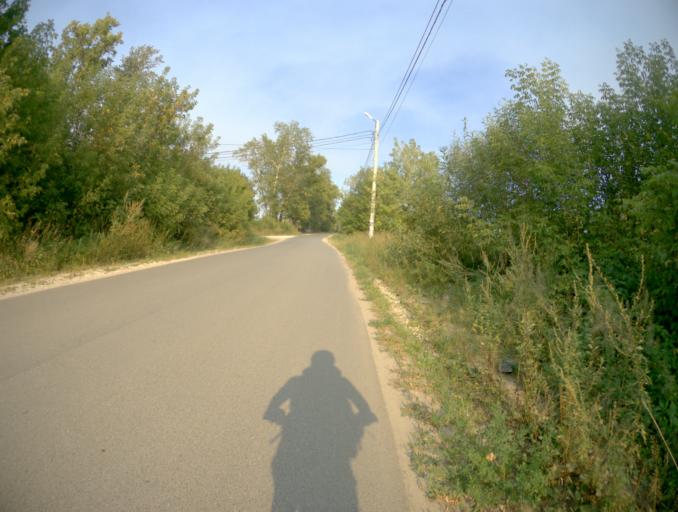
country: RU
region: Vladimir
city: Kosterevo
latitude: 55.9287
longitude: 39.6132
